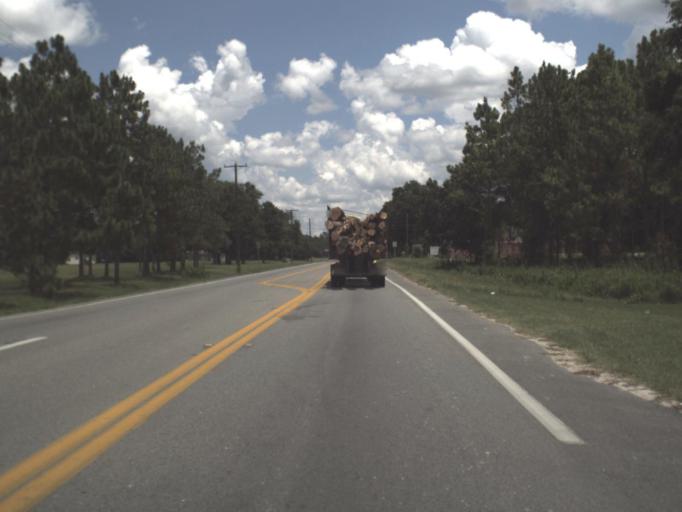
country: US
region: Florida
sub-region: Taylor County
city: Perry
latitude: 30.1095
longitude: -83.5958
